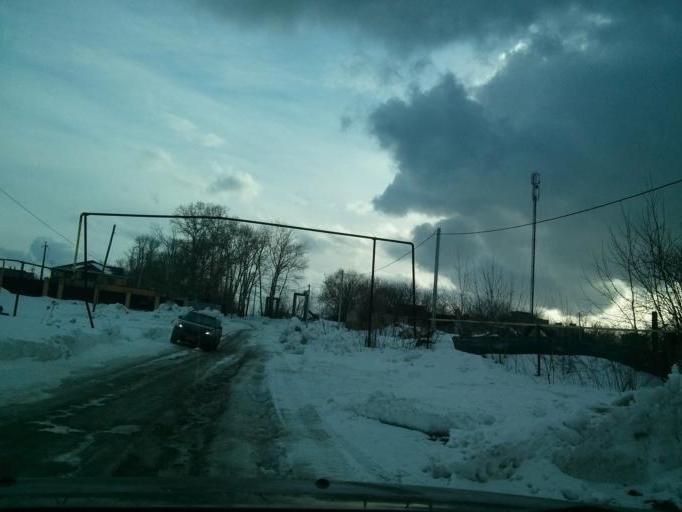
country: RU
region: Nizjnij Novgorod
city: Afonino
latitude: 56.2716
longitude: 44.0329
